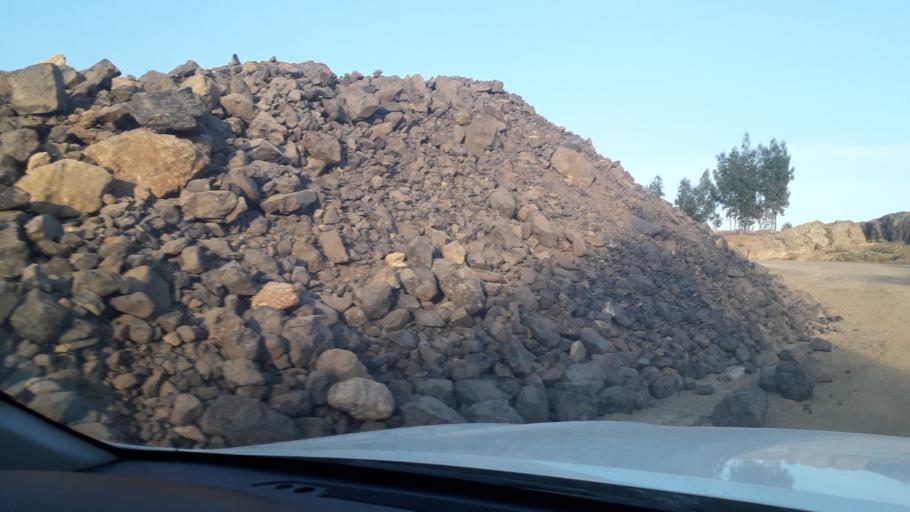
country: ET
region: Amhara
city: Lalibela
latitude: 11.5531
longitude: 39.2220
